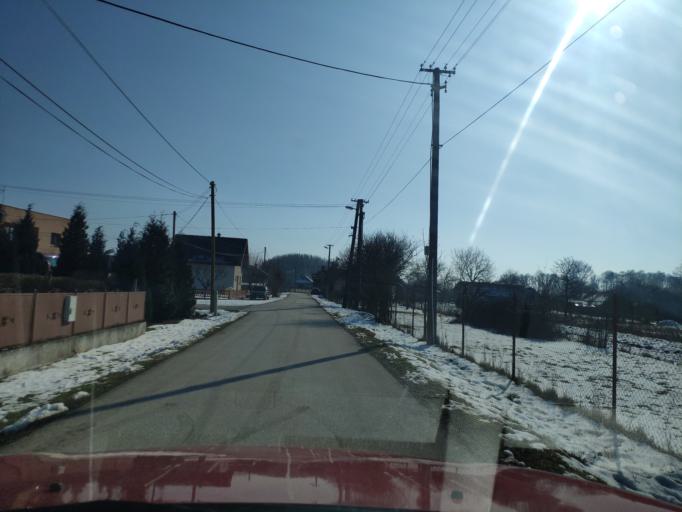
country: HU
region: Borsod-Abauj-Zemplen
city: Gonc
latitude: 48.5800
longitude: 21.2693
